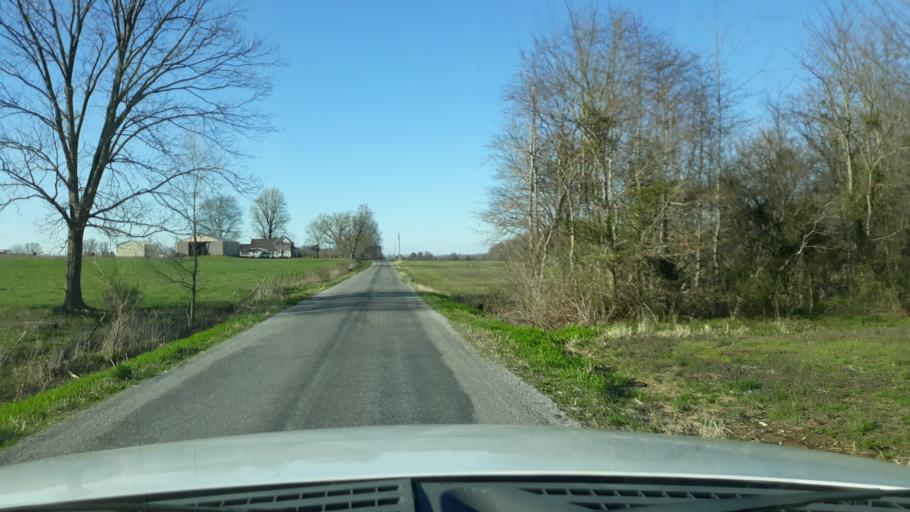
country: US
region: Illinois
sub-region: Saline County
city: Harrisburg
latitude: 37.7866
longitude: -88.6057
